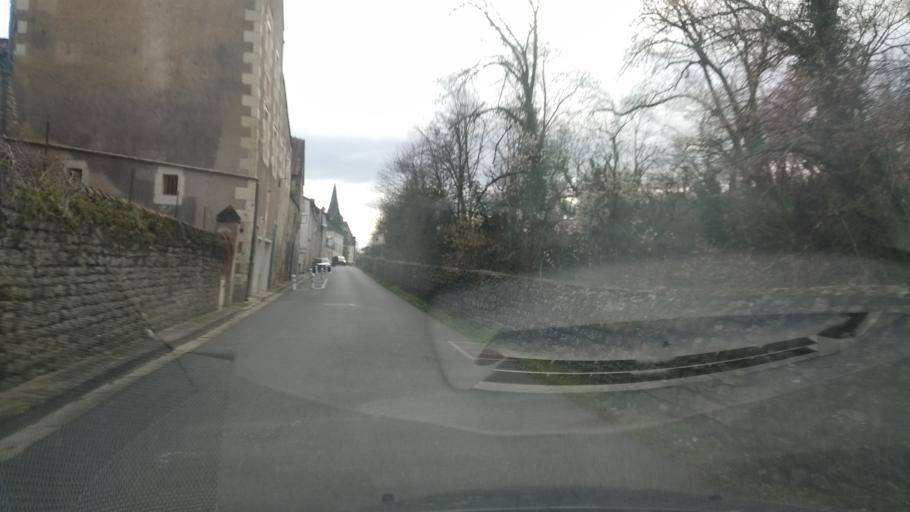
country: FR
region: Poitou-Charentes
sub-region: Departement de la Vienne
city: Dissay
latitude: 46.7024
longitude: 0.4322
